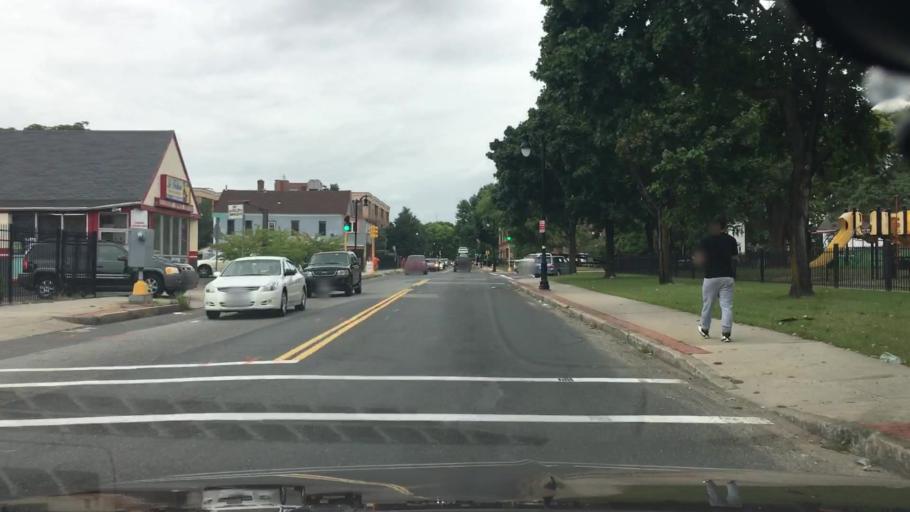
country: US
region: Massachusetts
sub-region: Hampden County
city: Springfield
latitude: 42.1051
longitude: -72.5728
